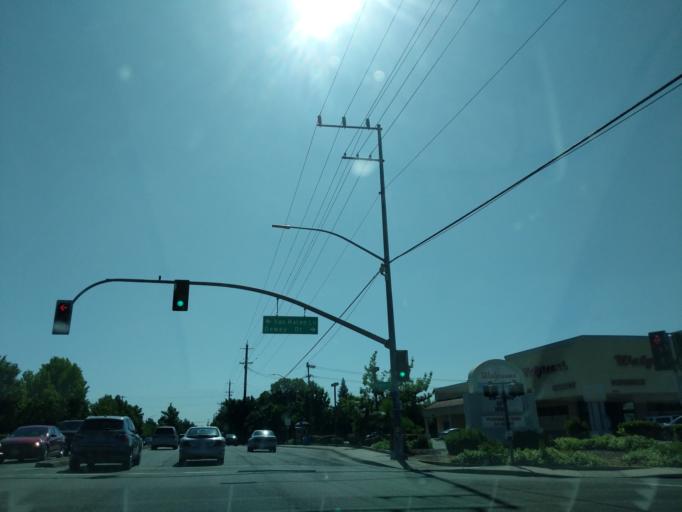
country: US
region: California
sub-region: Sacramento County
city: Antelope
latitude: 38.6781
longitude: -121.3104
